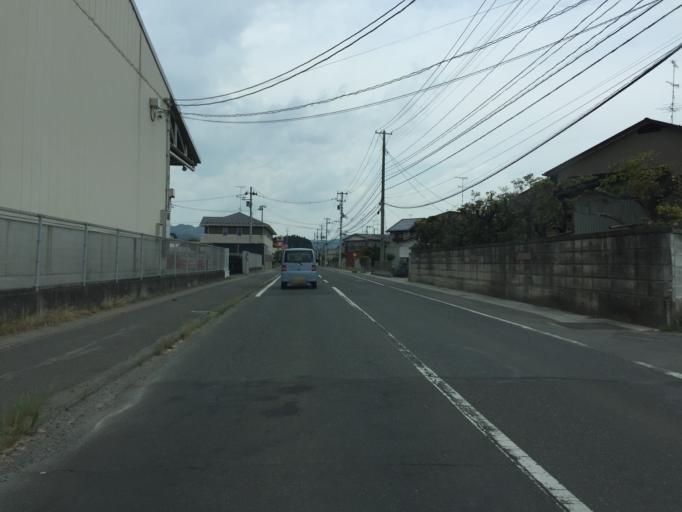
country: JP
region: Miyagi
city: Marumori
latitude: 37.8027
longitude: 140.9111
